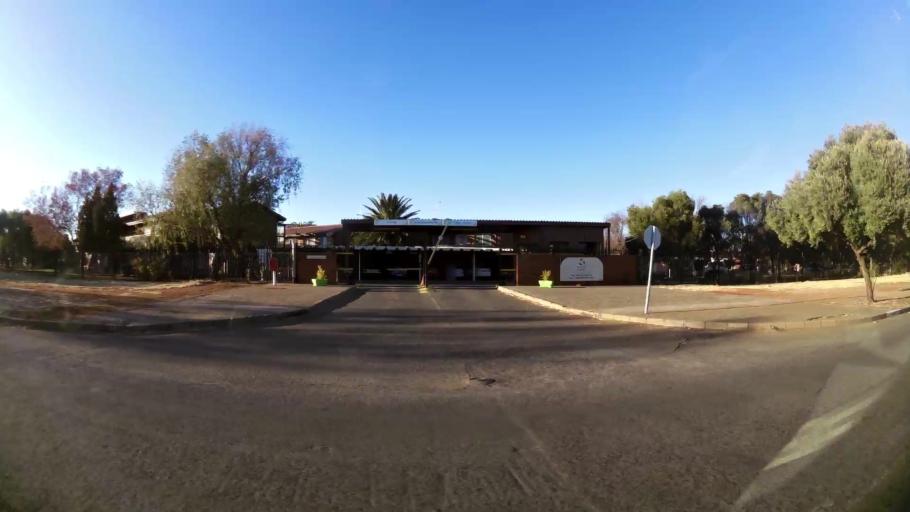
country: ZA
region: Northern Cape
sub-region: Frances Baard District Municipality
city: Kimberley
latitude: -28.7594
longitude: 24.7458
